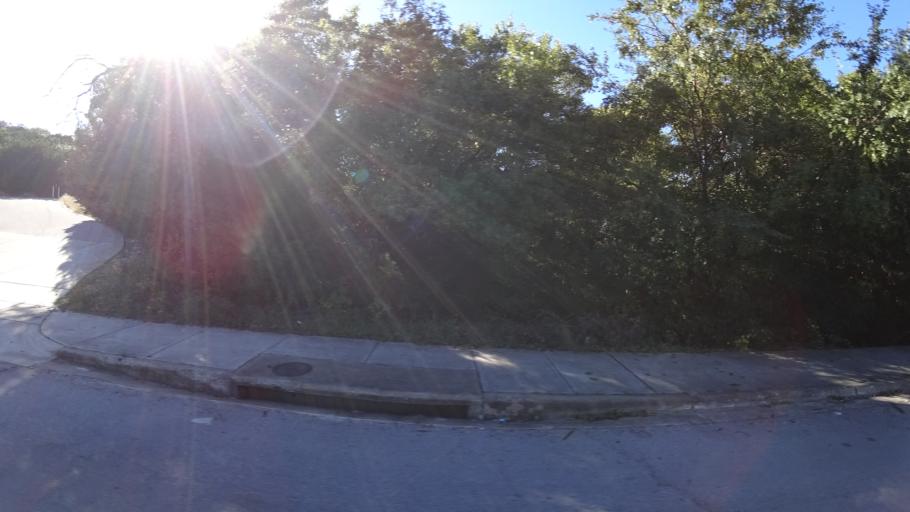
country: US
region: Texas
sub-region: Travis County
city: West Lake Hills
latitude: 30.3327
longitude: -97.8000
